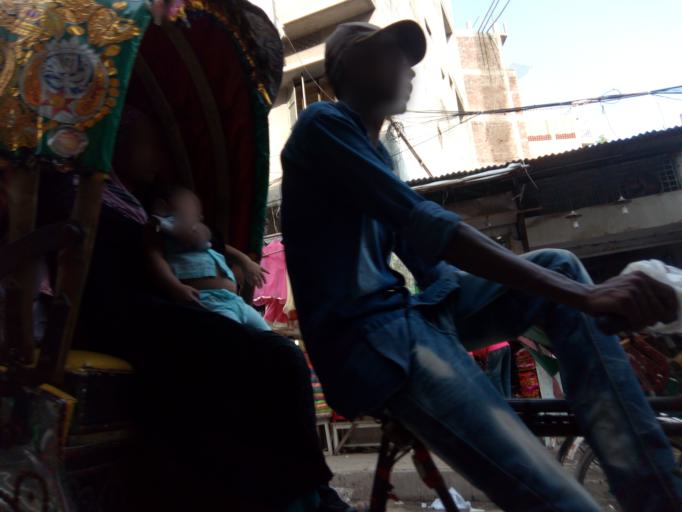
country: BD
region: Dhaka
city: Azimpur
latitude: 23.7178
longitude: 90.3863
